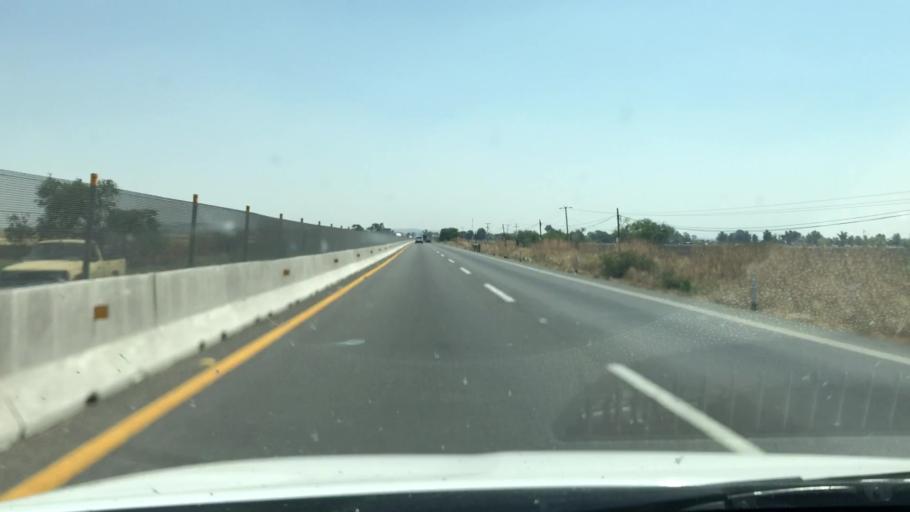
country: MX
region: Guanajuato
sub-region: Abasolo
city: San Bernardo Pena Blanca
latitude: 20.4769
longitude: -101.4990
